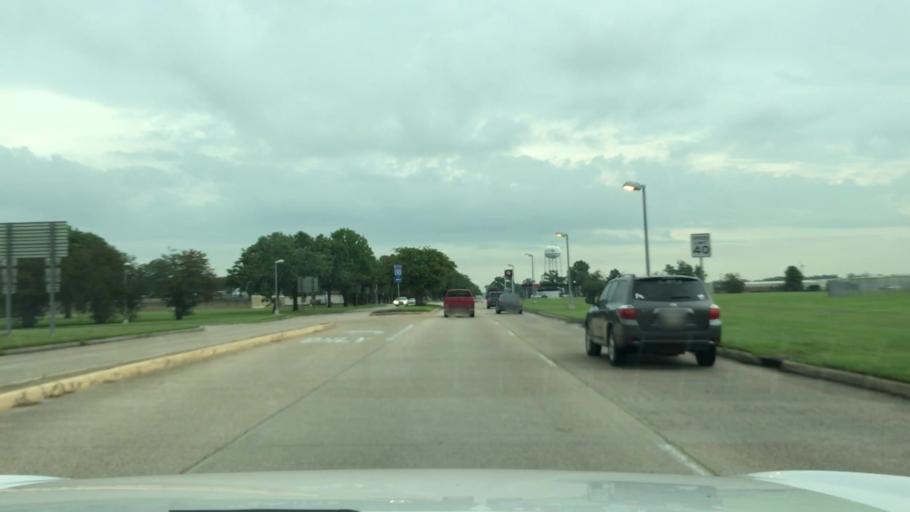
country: US
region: Louisiana
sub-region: East Baton Rouge Parish
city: Brownsfield
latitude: 30.5222
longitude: -91.1609
